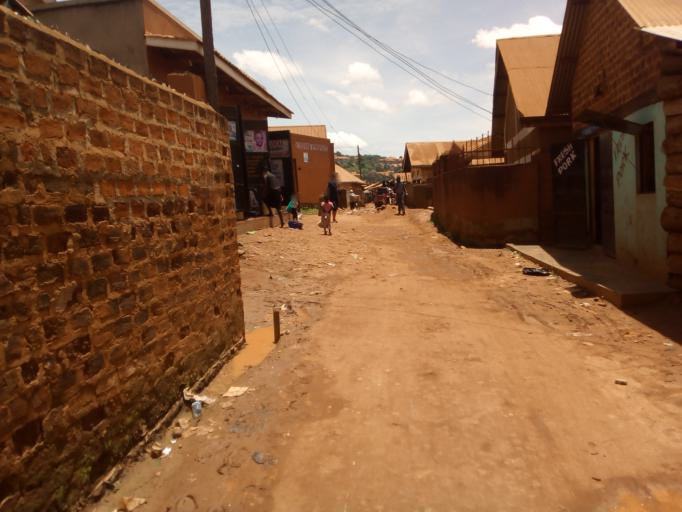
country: UG
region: Central Region
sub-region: Kampala District
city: Kampala
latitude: 0.2566
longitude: 32.5679
